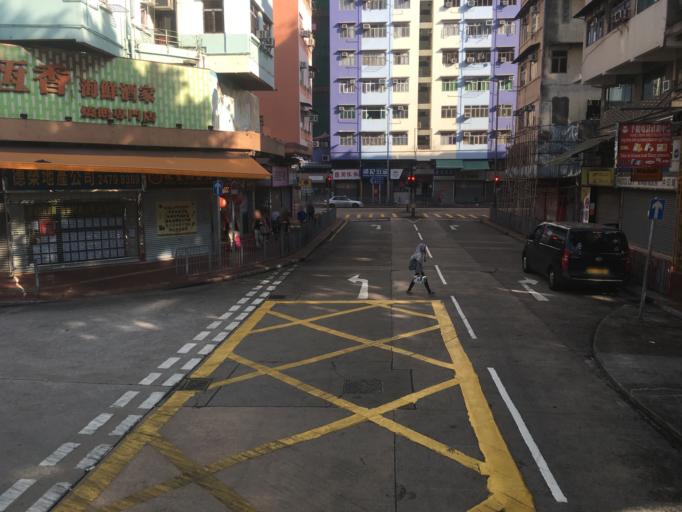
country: HK
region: Yuen Long
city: Yuen Long Kau Hui
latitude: 22.4455
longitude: 114.0251
